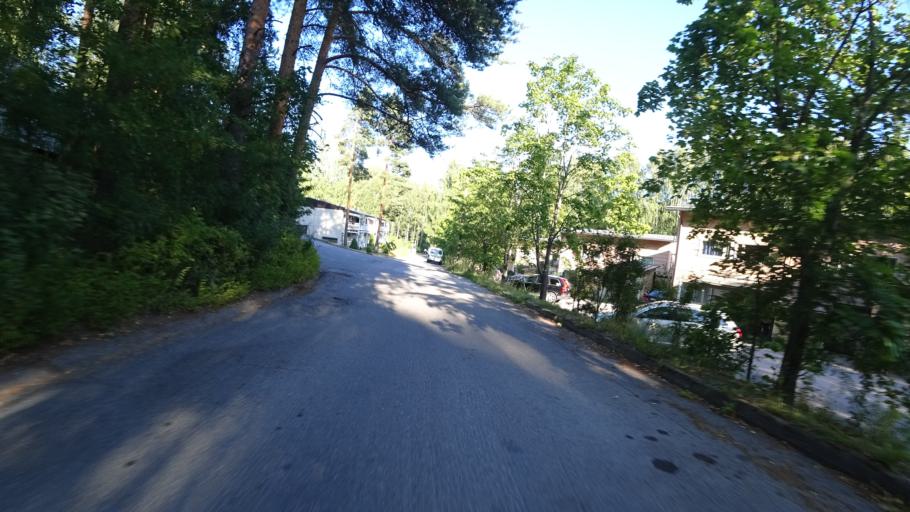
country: FI
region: Pirkanmaa
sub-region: Tampere
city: Pirkkala
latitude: 61.4947
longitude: 23.6126
